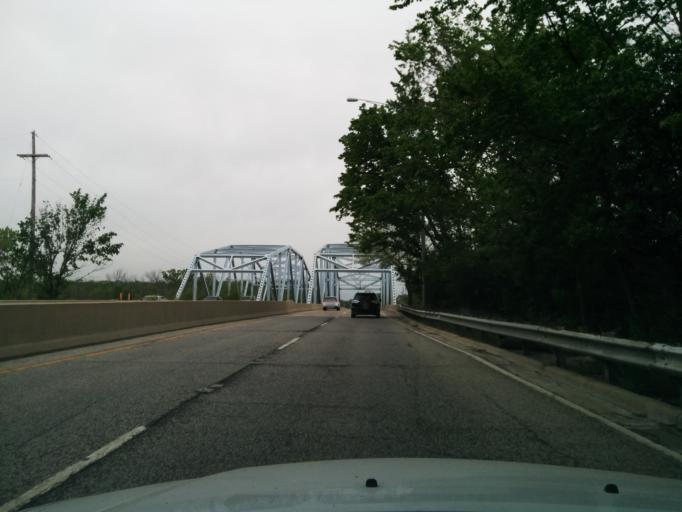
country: US
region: Illinois
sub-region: Cook County
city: Palos Park
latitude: 41.6846
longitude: -87.8552
